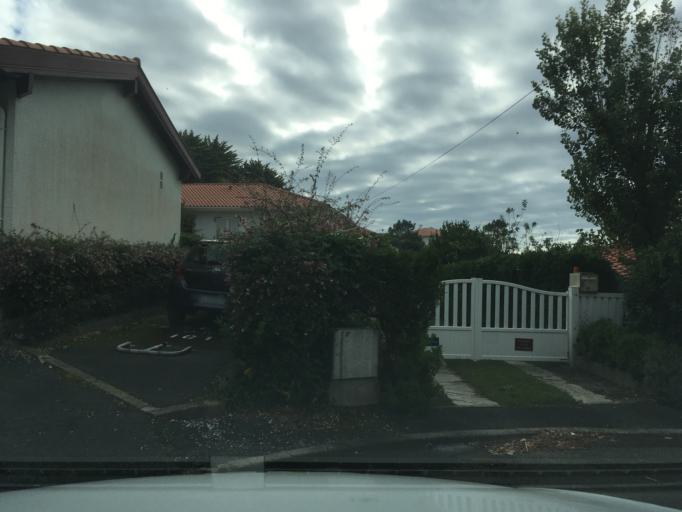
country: FR
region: Aquitaine
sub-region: Departement des Pyrenees-Atlantiques
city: Biarritz
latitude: 43.4657
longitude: -1.5680
